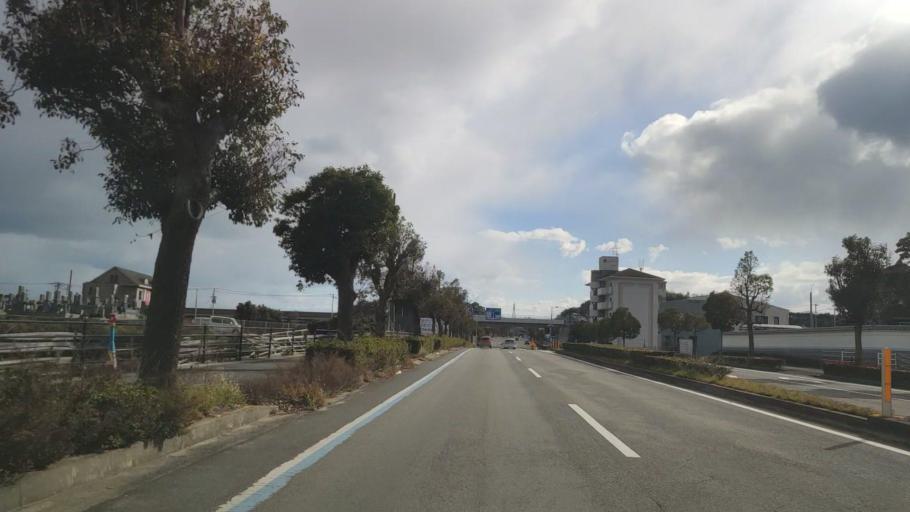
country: JP
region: Ehime
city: Hojo
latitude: 34.0592
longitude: 132.9689
